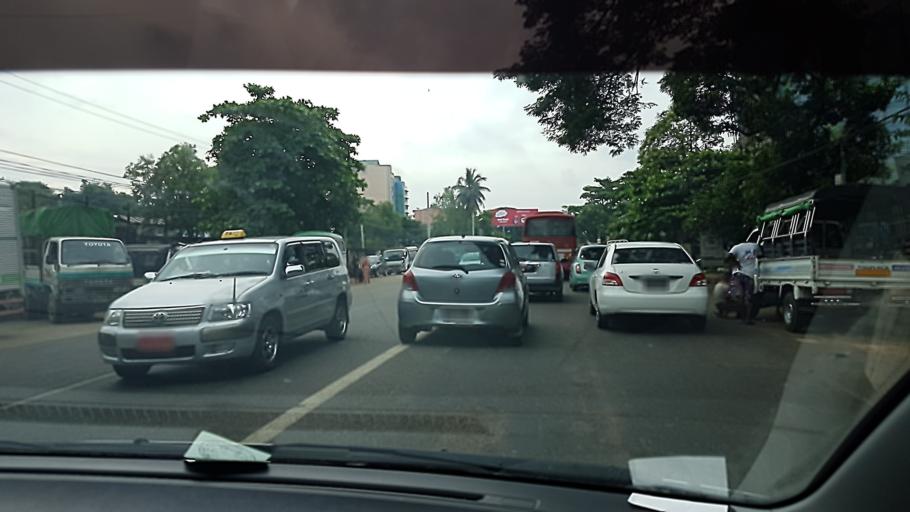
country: MM
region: Yangon
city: Yangon
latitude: 16.8139
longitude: 96.1260
